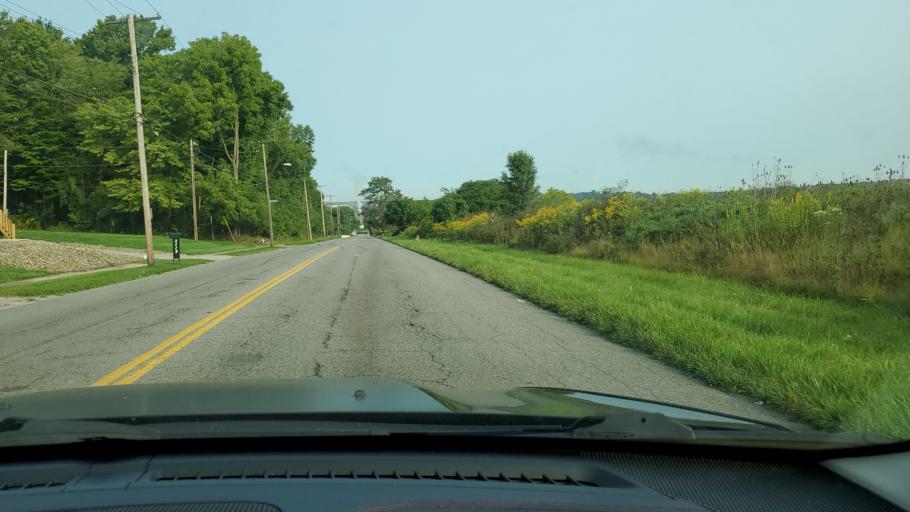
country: US
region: Ohio
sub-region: Mahoning County
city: Campbell
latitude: 41.0713
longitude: -80.6209
